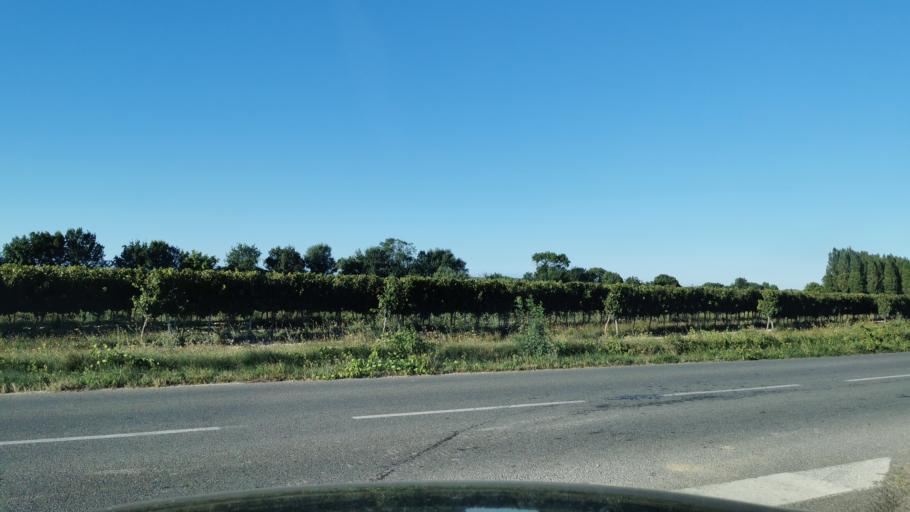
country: FR
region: Languedoc-Roussillon
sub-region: Departement de l'Aude
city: Coursan
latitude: 43.2456
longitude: 3.0172
